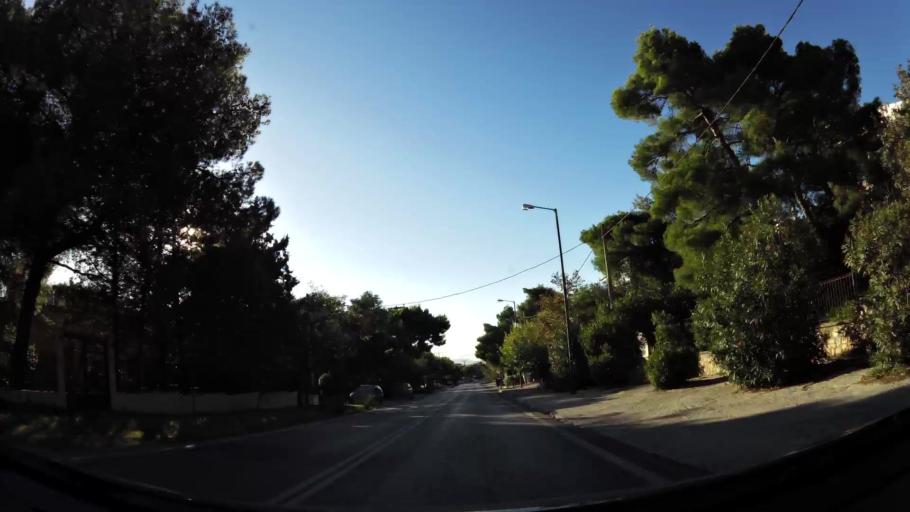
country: GR
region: Attica
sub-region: Nomarchia Athinas
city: Nea Penteli
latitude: 38.0525
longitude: 23.8577
